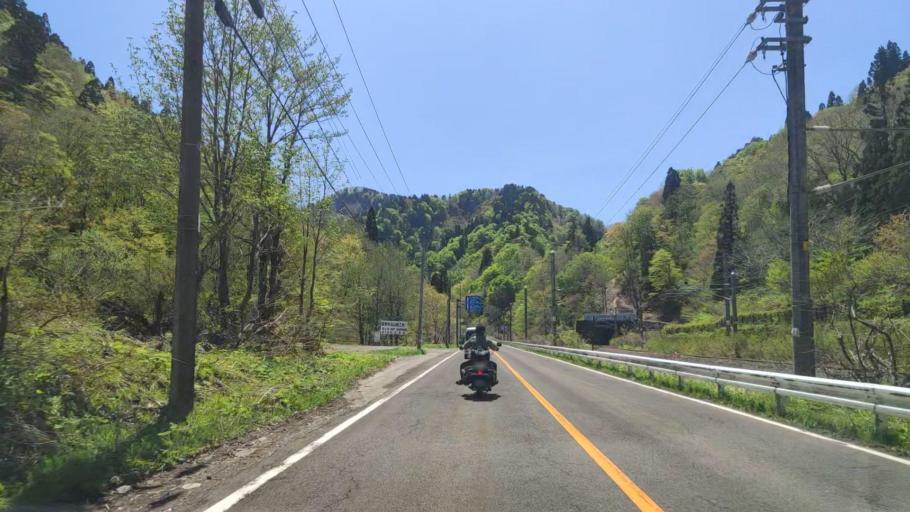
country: JP
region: Akita
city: Yuzawa
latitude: 39.0142
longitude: 140.3721
